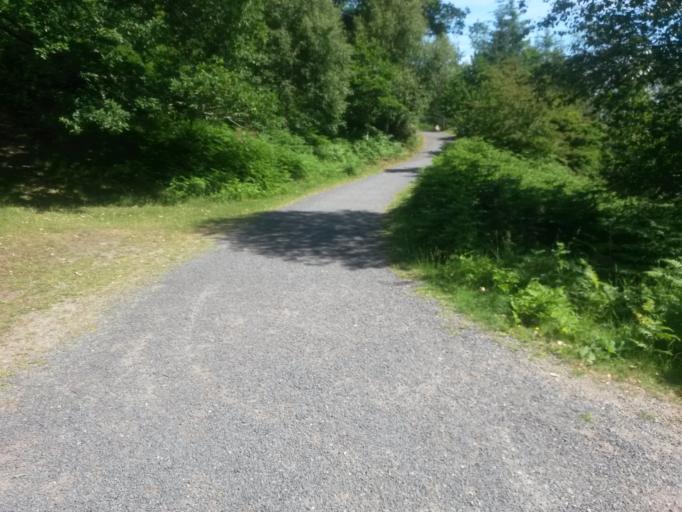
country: IE
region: Leinster
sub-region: Wicklow
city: Enniskerry
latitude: 53.1467
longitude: -6.2067
